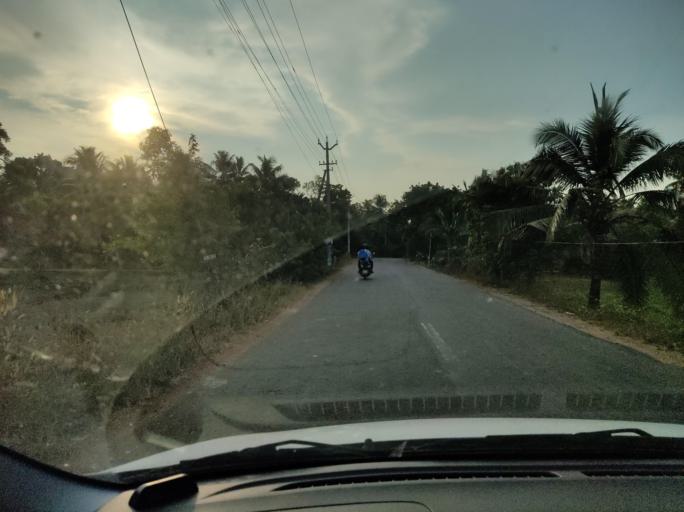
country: IN
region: Kerala
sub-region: Kottayam
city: Vaikam
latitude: 9.6854
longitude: 76.4374
